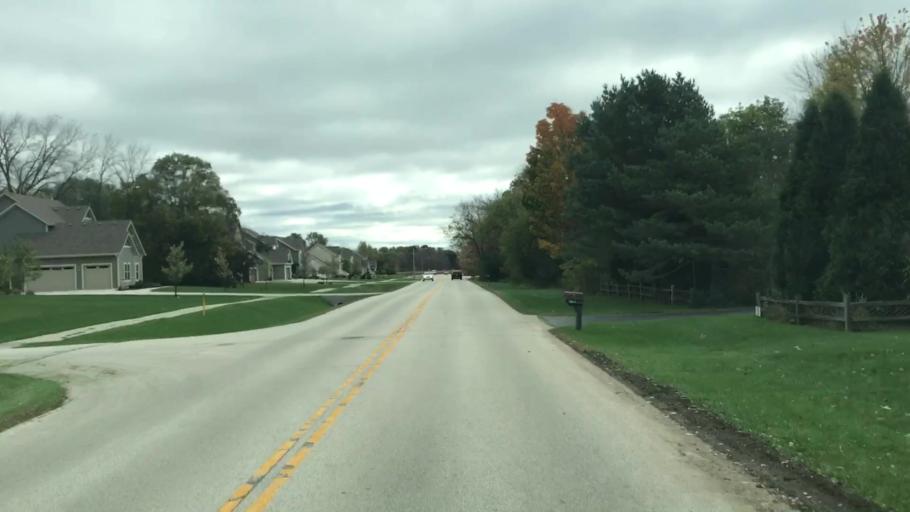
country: US
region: Wisconsin
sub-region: Waukesha County
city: Brookfield
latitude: 43.0757
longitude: -88.1314
